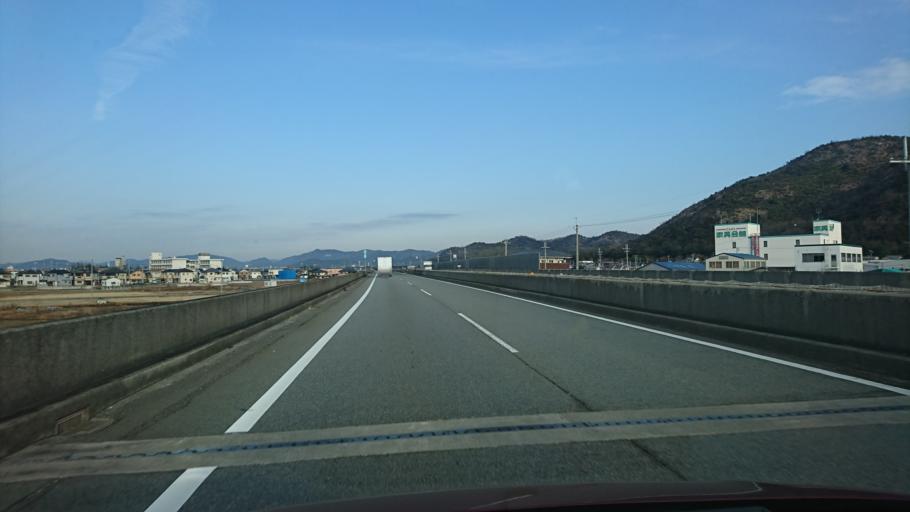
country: JP
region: Hyogo
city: Shirahamacho-usazakiminami
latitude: 34.8176
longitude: 134.7469
